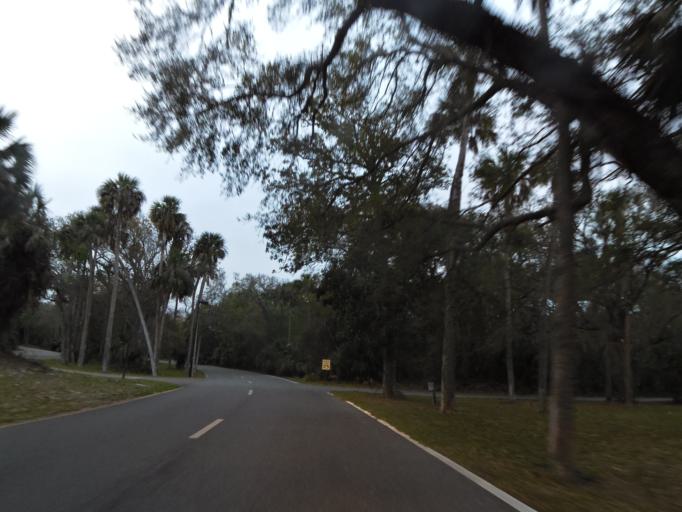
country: US
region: Florida
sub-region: Duval County
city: Atlantic Beach
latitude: 30.3715
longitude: -81.4008
